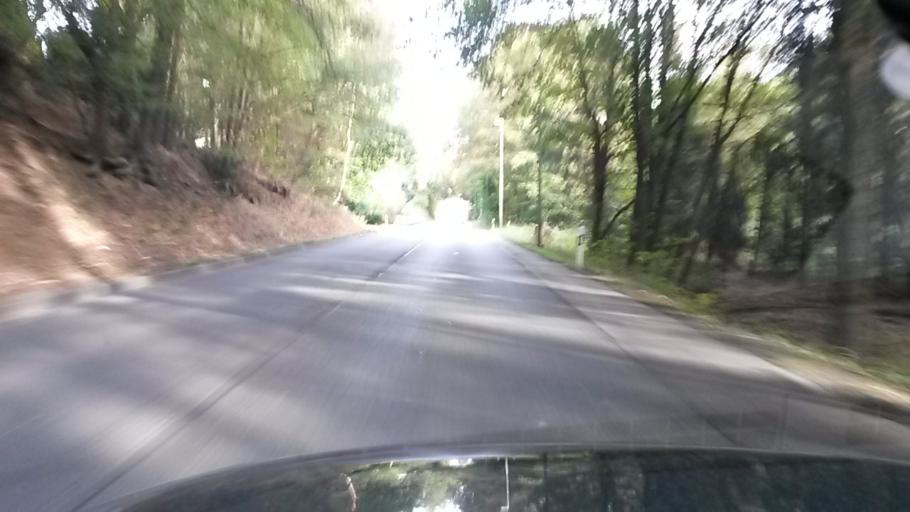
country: DE
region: North Rhine-Westphalia
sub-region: Regierungsbezirk Arnsberg
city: Luedenscheid
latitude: 51.2324
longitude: 7.6786
